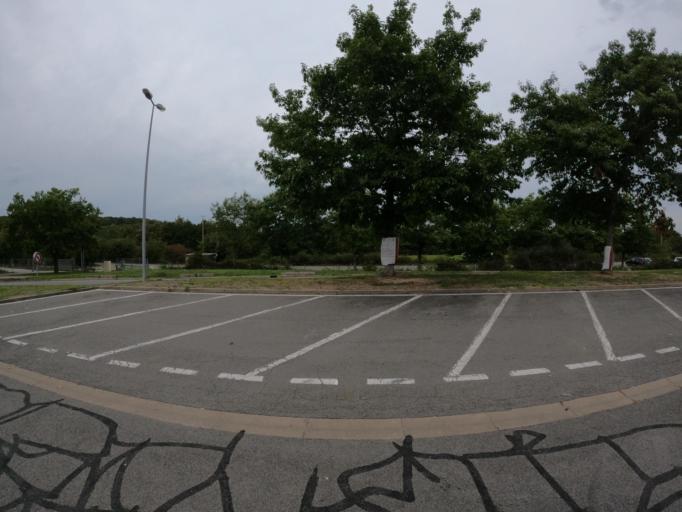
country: FR
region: Auvergne
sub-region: Departement de l'Allier
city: Doyet
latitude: 46.3572
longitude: 2.8023
